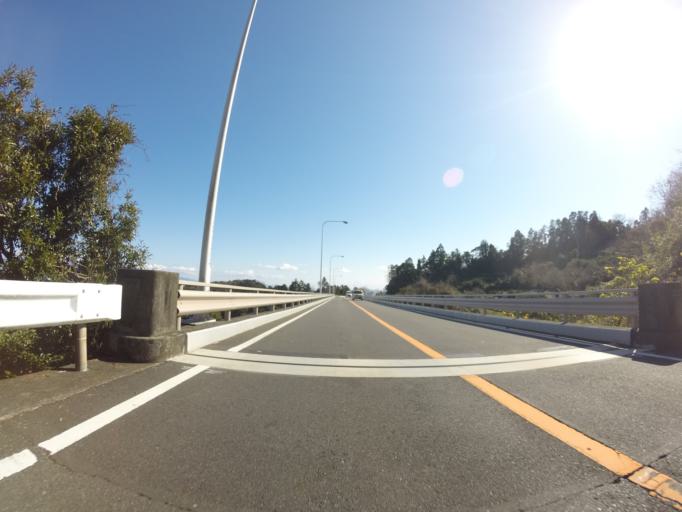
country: JP
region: Shizuoka
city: Shizuoka-shi
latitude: 34.9756
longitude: 138.4747
